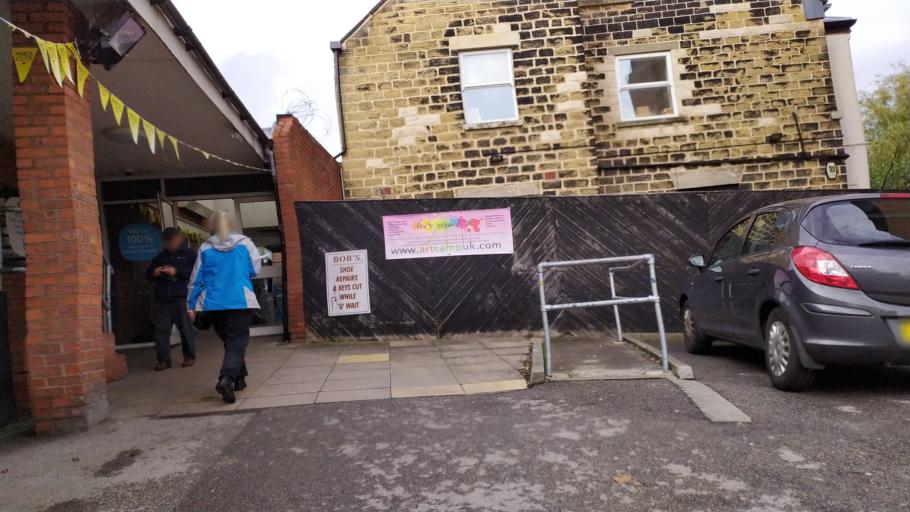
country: GB
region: England
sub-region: City and Borough of Leeds
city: Chapel Allerton
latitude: 53.8285
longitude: -1.5387
